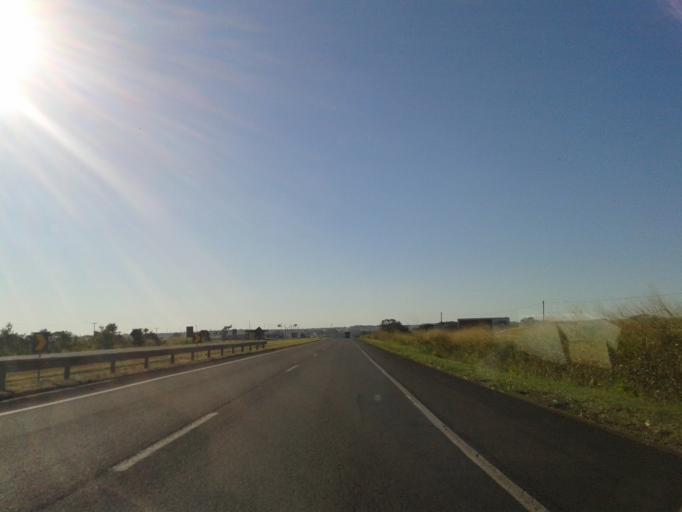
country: BR
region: Minas Gerais
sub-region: Uberlandia
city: Uberlandia
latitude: -19.0101
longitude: -48.2083
